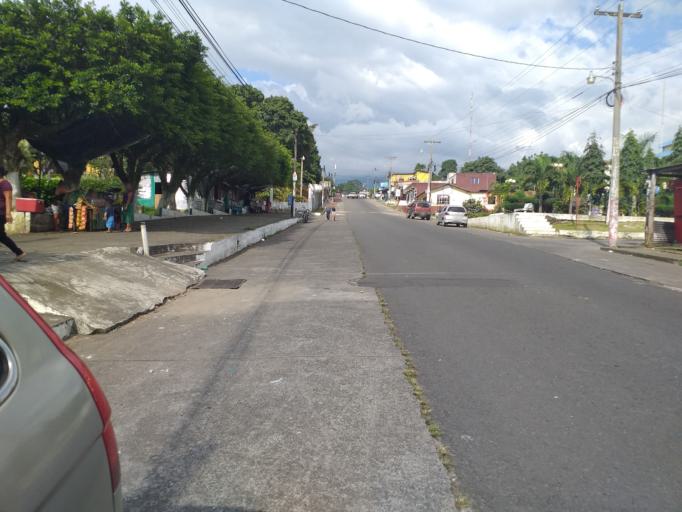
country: GT
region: Suchitepeque
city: Pueblo Nuevo
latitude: 14.6460
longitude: -91.5557
